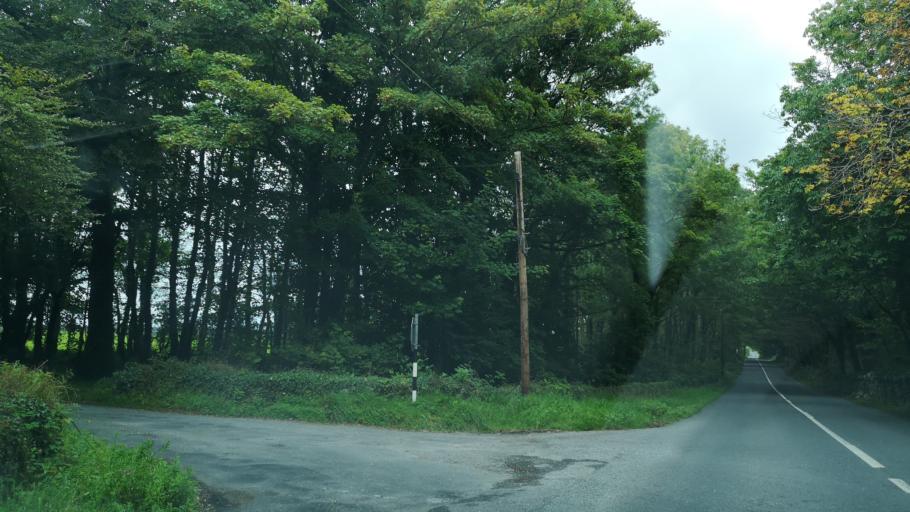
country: IE
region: Connaught
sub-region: County Galway
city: Athenry
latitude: 53.3349
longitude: -8.7705
